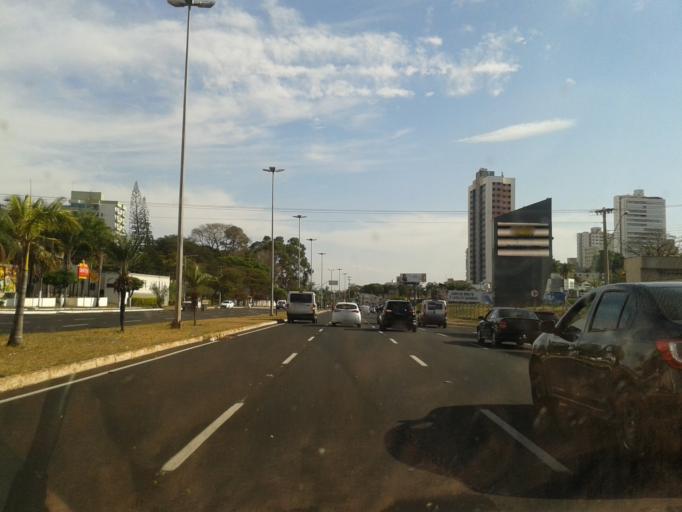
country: BR
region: Minas Gerais
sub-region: Uberlandia
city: Uberlandia
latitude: -18.9206
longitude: -48.2684
